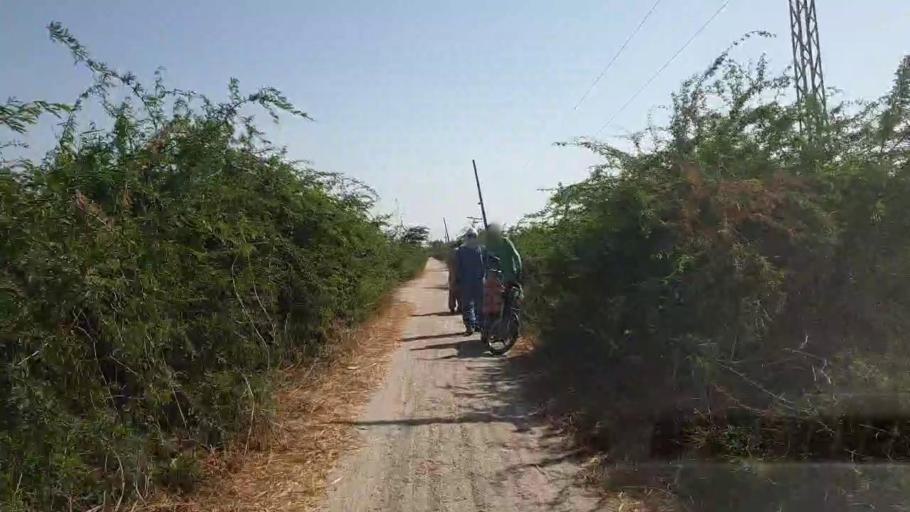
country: PK
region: Sindh
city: Tando Bago
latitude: 24.6449
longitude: 68.9870
